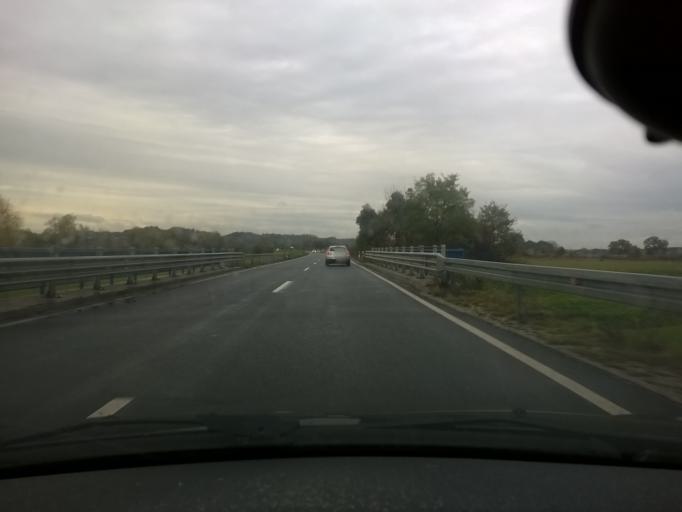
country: HR
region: Zagrebacka
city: Jakovlje
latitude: 45.9421
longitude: 15.8232
